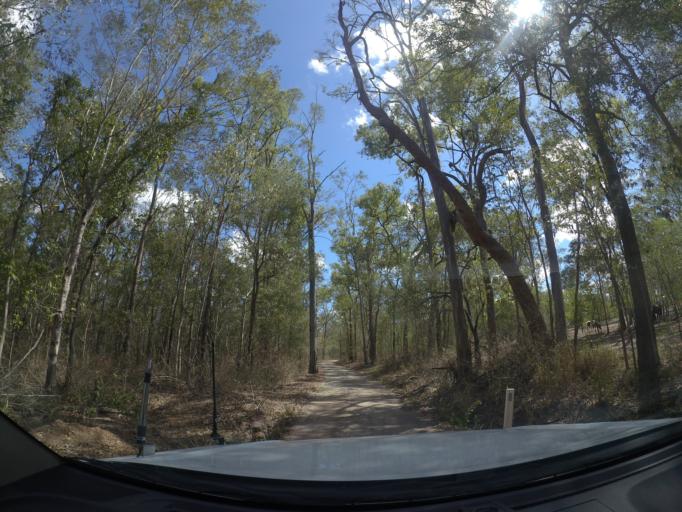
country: AU
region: Queensland
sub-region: Logan
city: North Maclean
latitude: -27.8215
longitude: 152.9692
